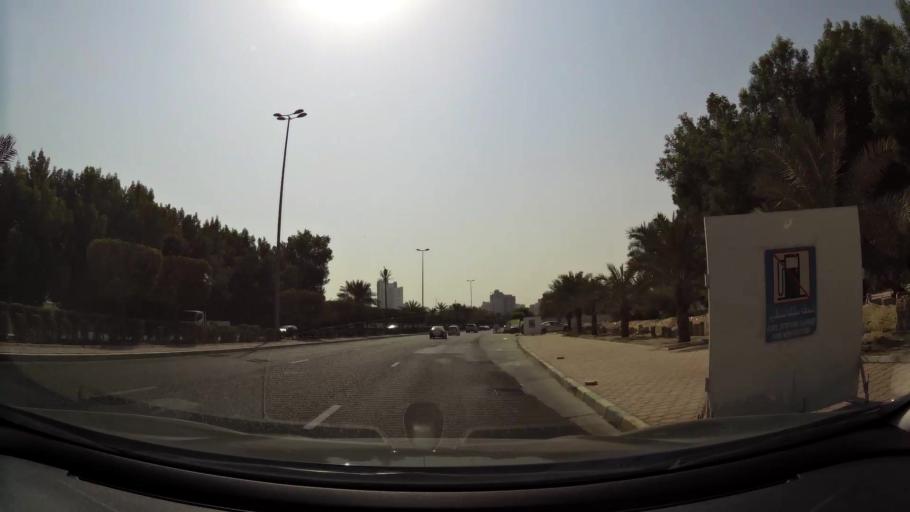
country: KW
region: Al Ahmadi
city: Al Fintas
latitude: 29.1651
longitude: 48.1231
